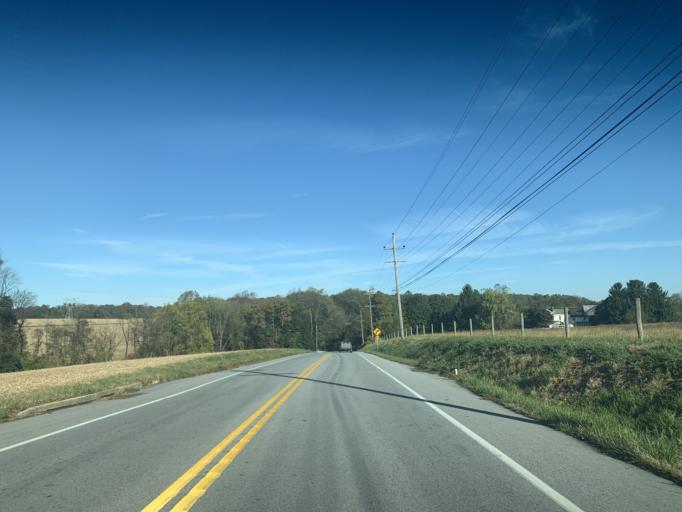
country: US
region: Pennsylvania
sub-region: Chester County
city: Parkesburg
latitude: 39.9426
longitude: -75.9136
